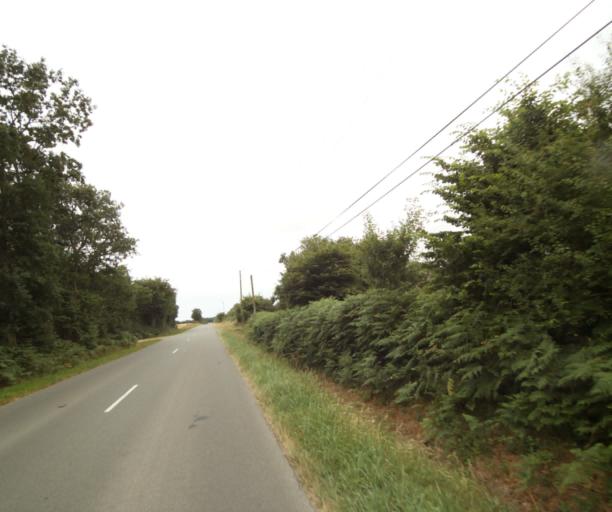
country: FR
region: Pays de la Loire
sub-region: Departement de la Vendee
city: Chateau-d'Olonne
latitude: 46.5009
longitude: -1.6941
